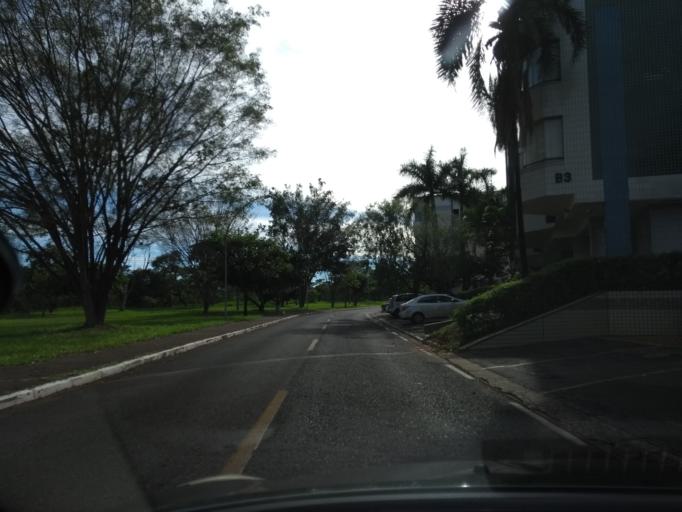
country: BR
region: Federal District
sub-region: Brasilia
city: Brasilia
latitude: -15.7829
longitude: -47.9286
